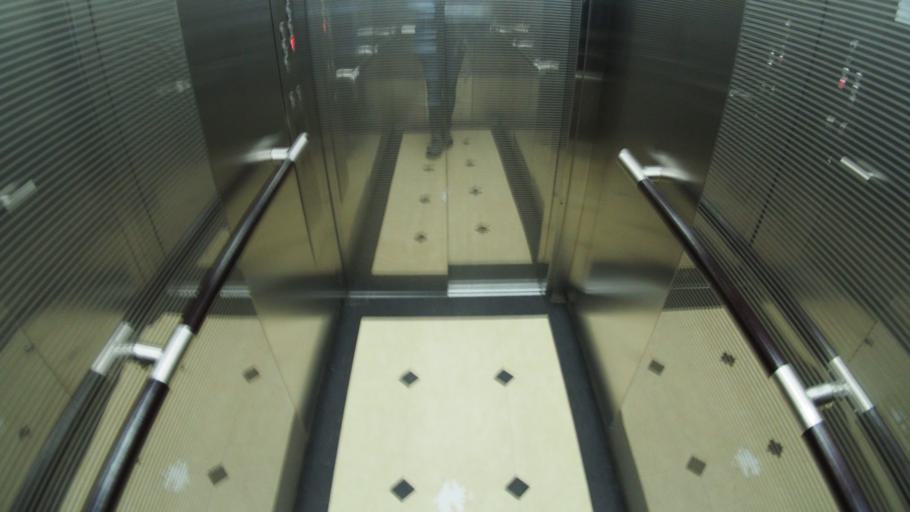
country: RU
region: Primorskiy
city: Russkiy
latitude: 43.0278
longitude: 131.8888
